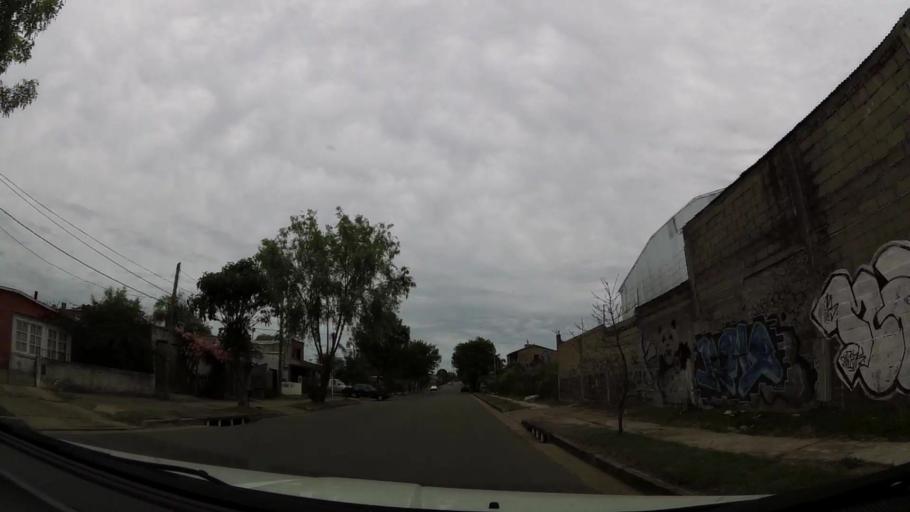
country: UY
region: Maldonado
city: Maldonado
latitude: -34.8898
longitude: -54.9403
